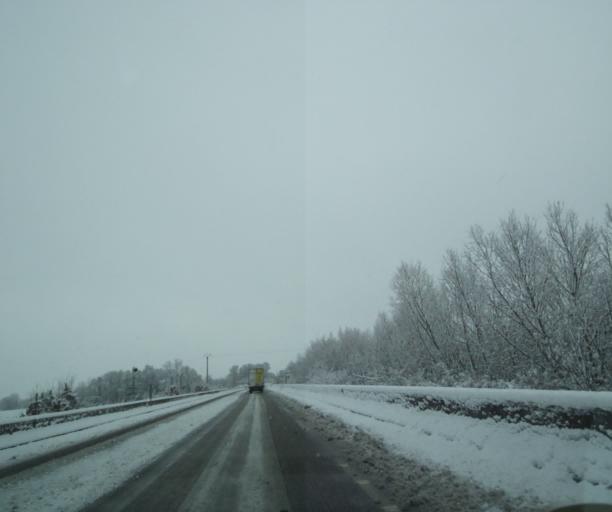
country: FR
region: Champagne-Ardenne
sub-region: Departement de la Haute-Marne
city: Saint-Dizier
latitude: 48.5892
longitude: 4.8907
